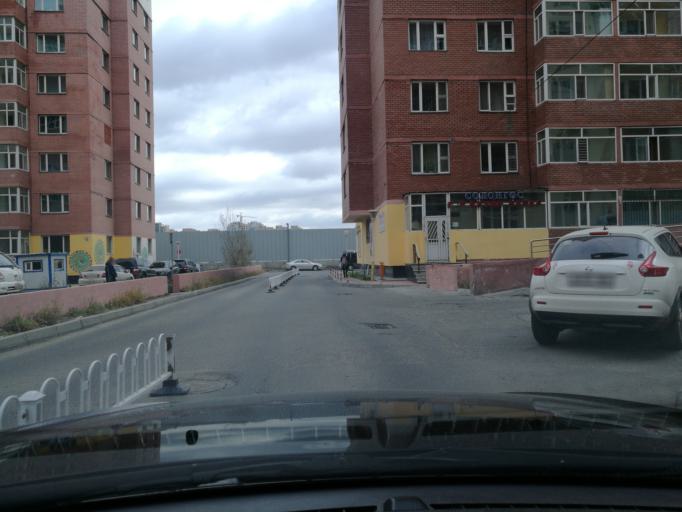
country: MN
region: Ulaanbaatar
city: Ulaanbaatar
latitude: 47.9006
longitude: 106.9196
